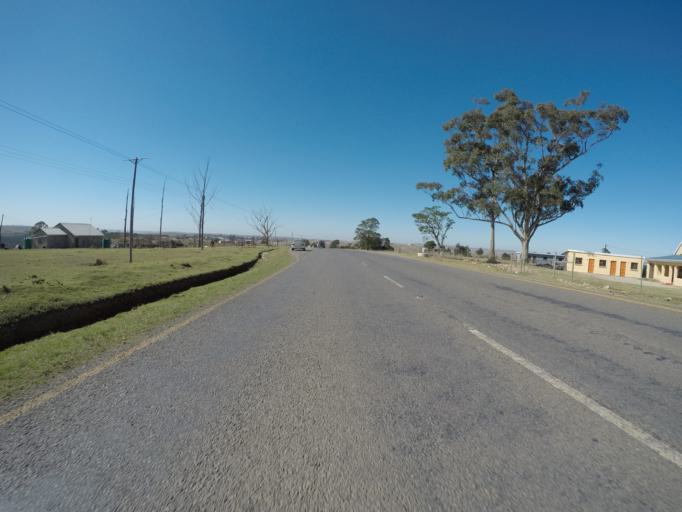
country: ZA
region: Eastern Cape
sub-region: OR Tambo District Municipality
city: Mthatha
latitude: -31.7966
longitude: 28.7450
